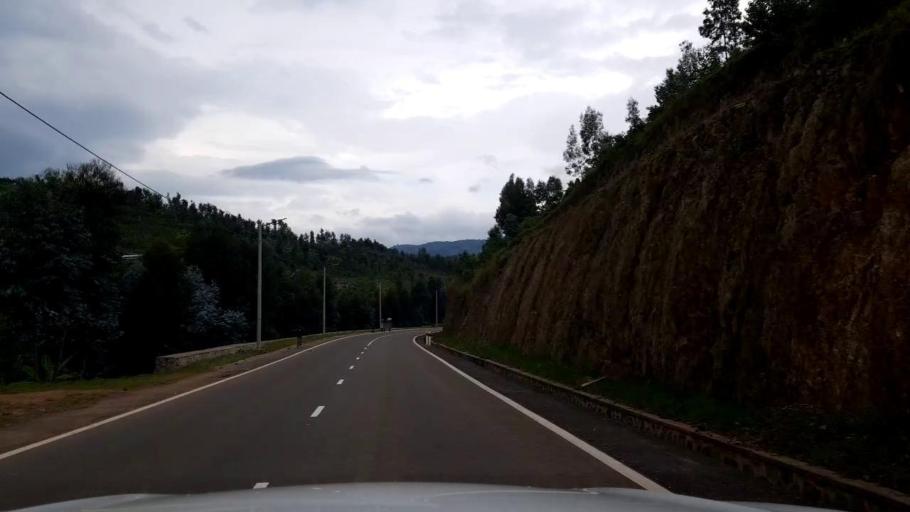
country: RW
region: Western Province
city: Kibuye
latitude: -2.0221
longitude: 29.3881
